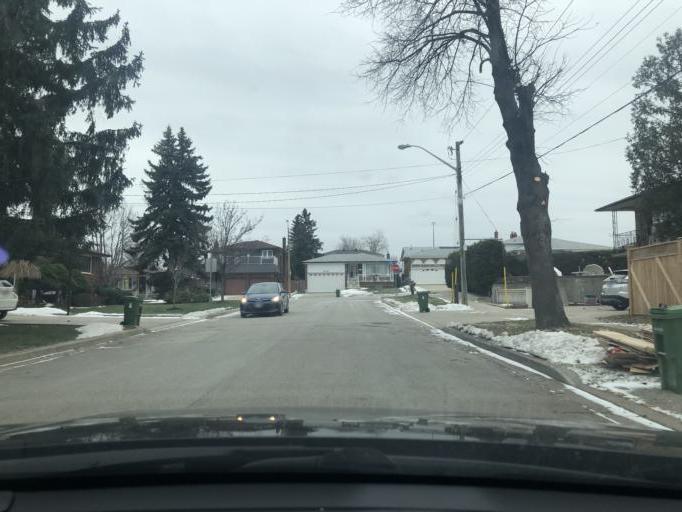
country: CA
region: Ontario
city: Scarborough
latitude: 43.7734
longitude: -79.3021
